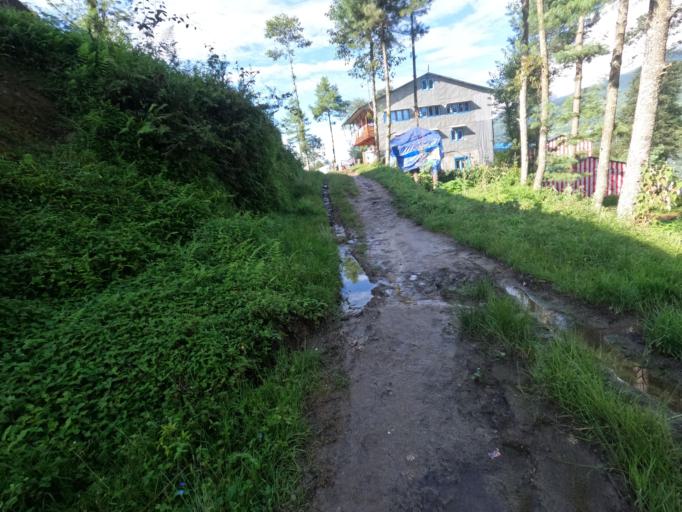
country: NP
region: Eastern Region
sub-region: Sagarmatha Zone
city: Namche Bazar
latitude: 27.4918
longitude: 86.5818
